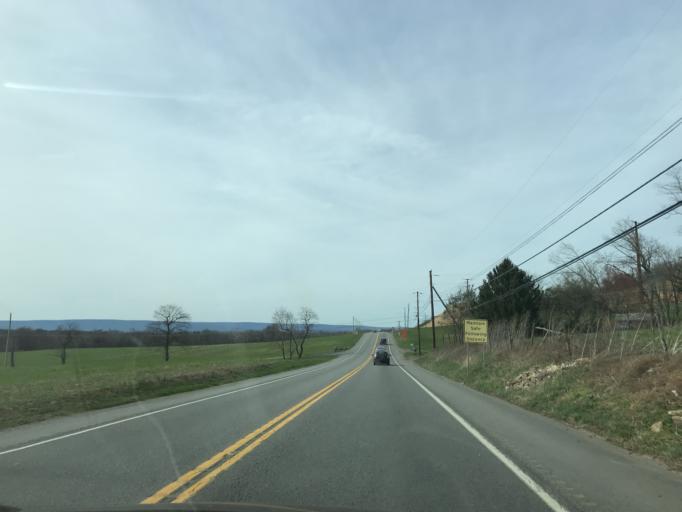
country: US
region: Pennsylvania
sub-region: Union County
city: Lewisburg
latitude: 40.9310
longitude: -76.8482
